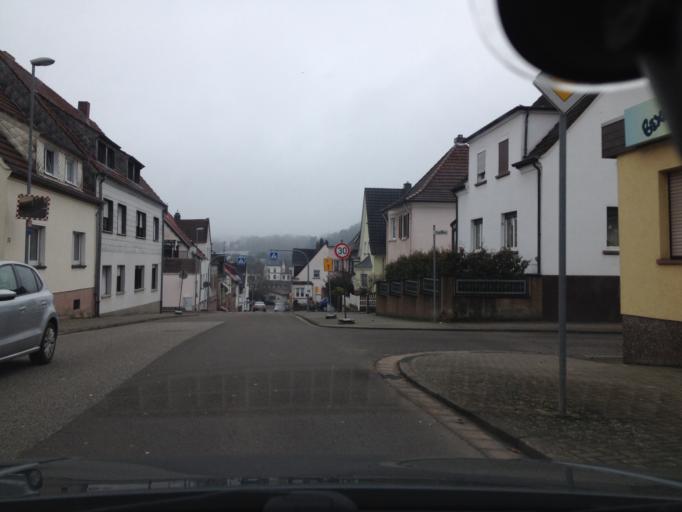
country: DE
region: Saarland
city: Bexbach
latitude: 49.3488
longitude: 7.2522
